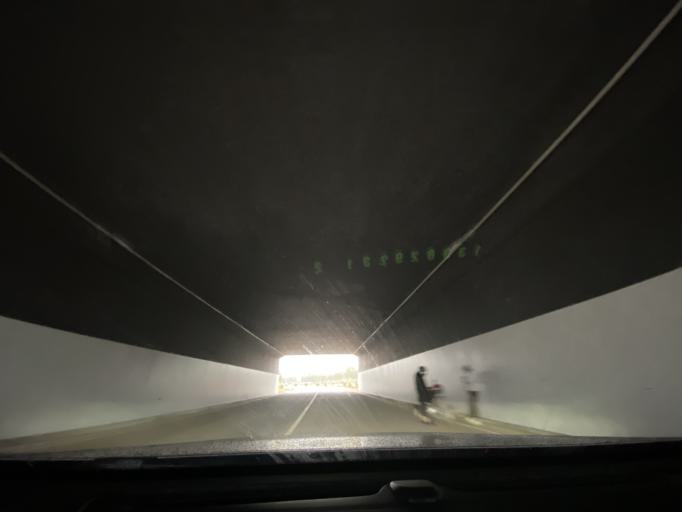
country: CN
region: Sichuan
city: Jiancheng
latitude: 30.3948
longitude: 104.6337
